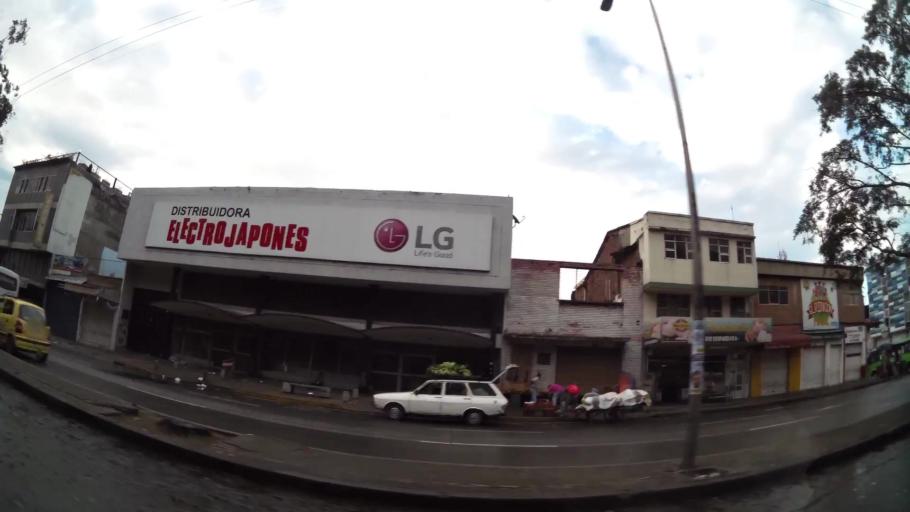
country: CO
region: Valle del Cauca
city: Cali
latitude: 3.4470
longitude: -76.5324
